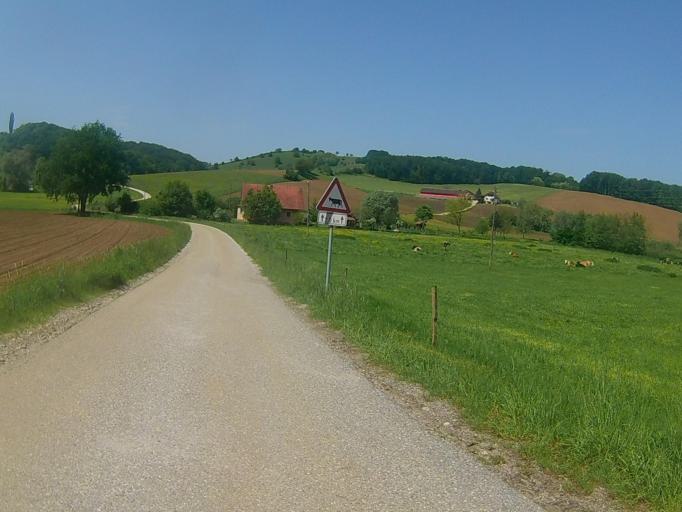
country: SI
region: Sveti Jurij v Slovenskih Goricah
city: Jurovski Dol
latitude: 46.5977
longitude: 15.7433
